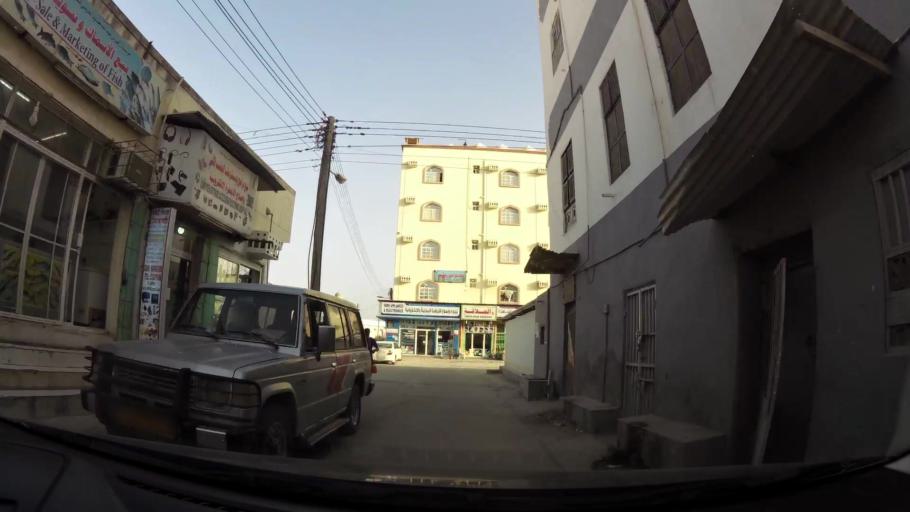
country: OM
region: Zufar
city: Salalah
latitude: 17.0127
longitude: 54.0977
